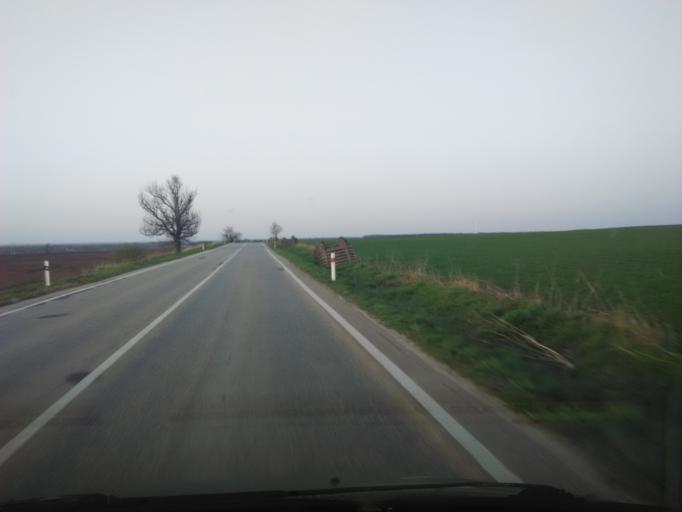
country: SK
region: Nitriansky
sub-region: Okres Nitra
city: Nitra
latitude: 48.2342
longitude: 18.0055
